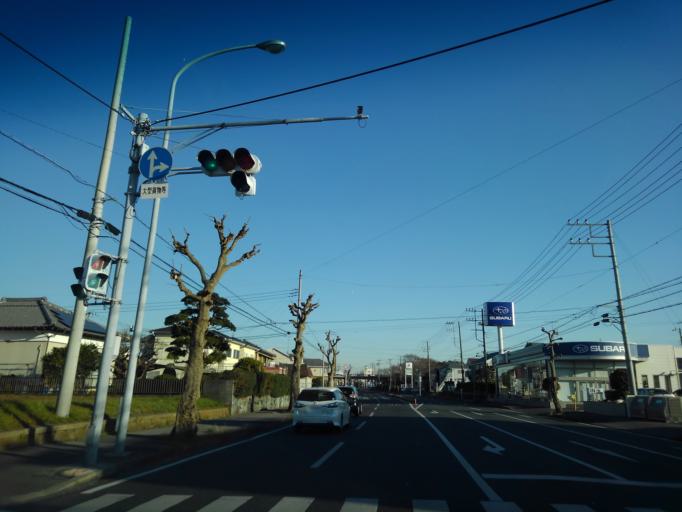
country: JP
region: Chiba
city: Kimitsu
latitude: 35.3196
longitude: 139.9167
